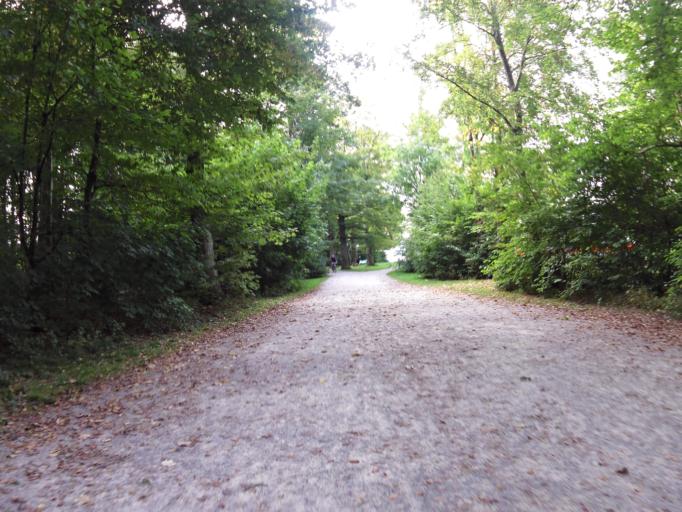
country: DE
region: Bavaria
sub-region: Upper Bavaria
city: Starnberg
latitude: 47.9940
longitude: 11.3592
